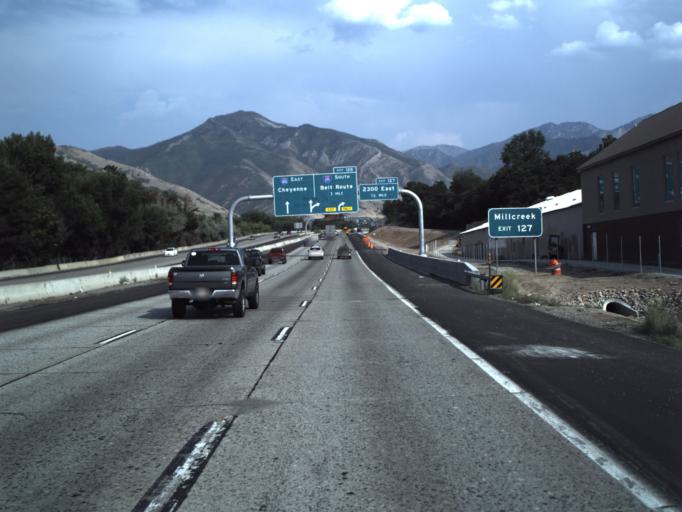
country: US
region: Utah
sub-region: Salt Lake County
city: Willard
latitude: 40.7183
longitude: -111.8405
